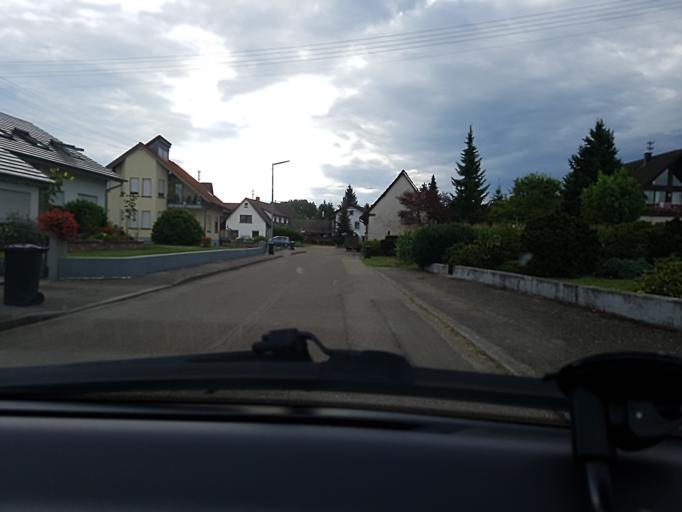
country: DE
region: Baden-Wuerttemberg
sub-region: Freiburg Region
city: Offenburg
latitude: 48.4851
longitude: 7.9109
